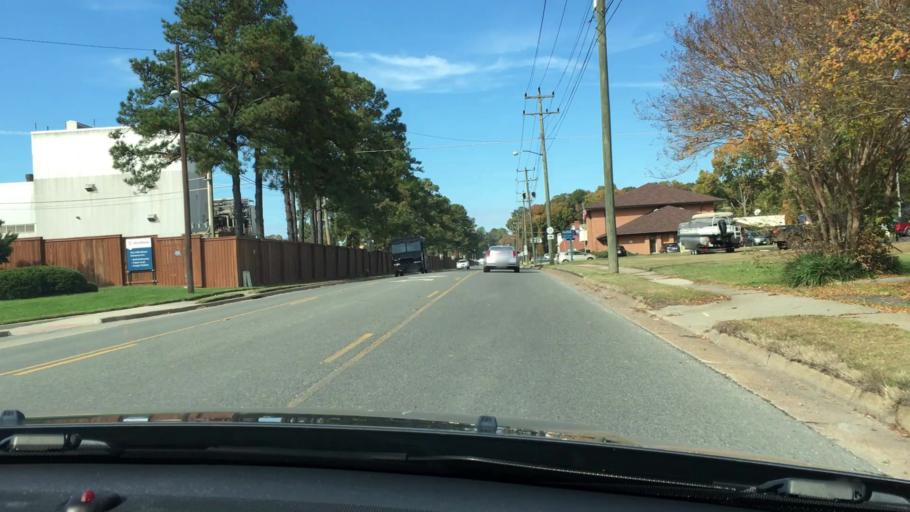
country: US
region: Virginia
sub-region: King William County
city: West Point
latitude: 37.5408
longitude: -76.8014
